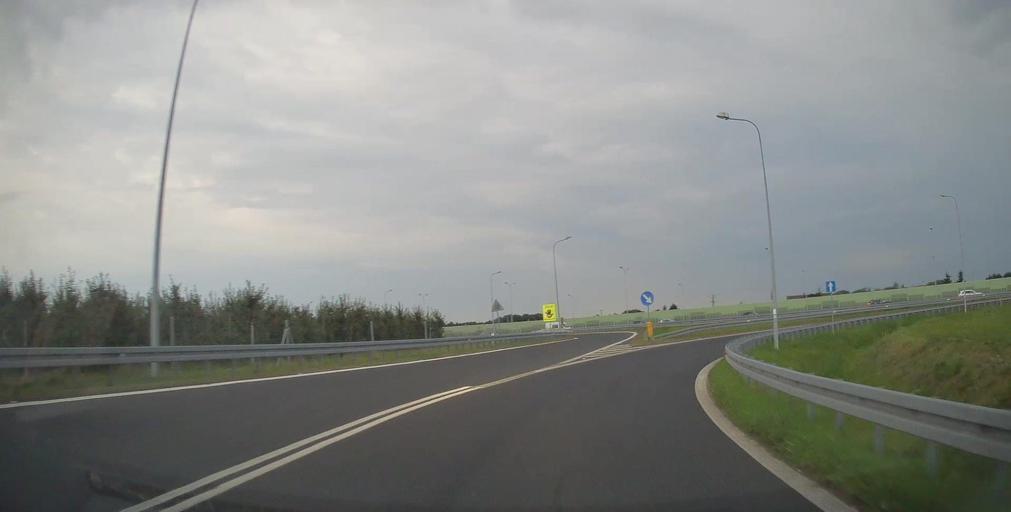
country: PL
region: Masovian Voivodeship
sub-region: Powiat grojecki
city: Grojec
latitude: 51.8266
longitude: 20.8813
